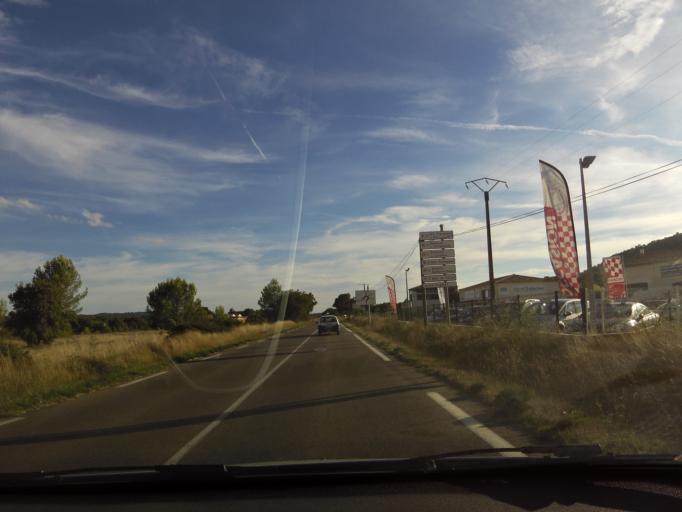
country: FR
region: Languedoc-Roussillon
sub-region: Departement de l'Herault
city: Claret
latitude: 43.8448
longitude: 3.9200
